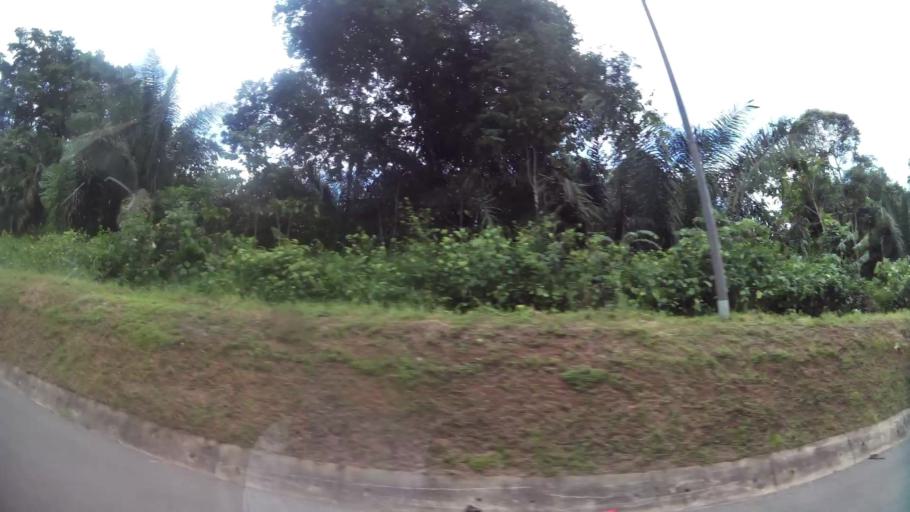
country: PA
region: Panama
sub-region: Distrito Arraijan
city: Arraijan
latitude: 8.9772
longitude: -79.6453
